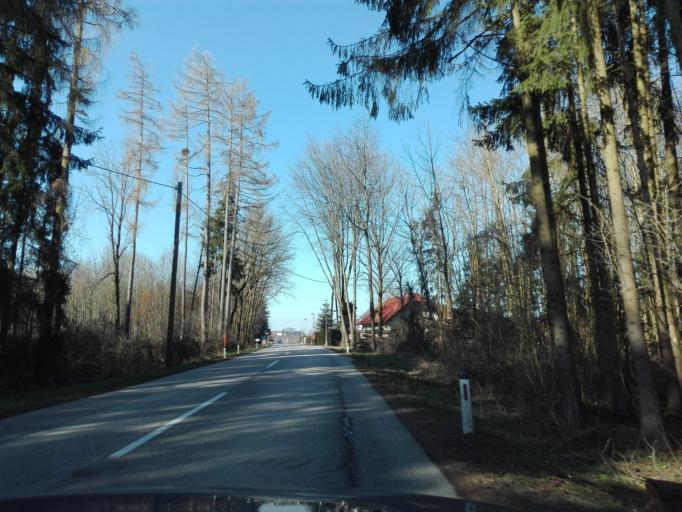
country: AT
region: Upper Austria
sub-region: Wels-Land
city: Holzhausen
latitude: 48.2431
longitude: 14.1205
